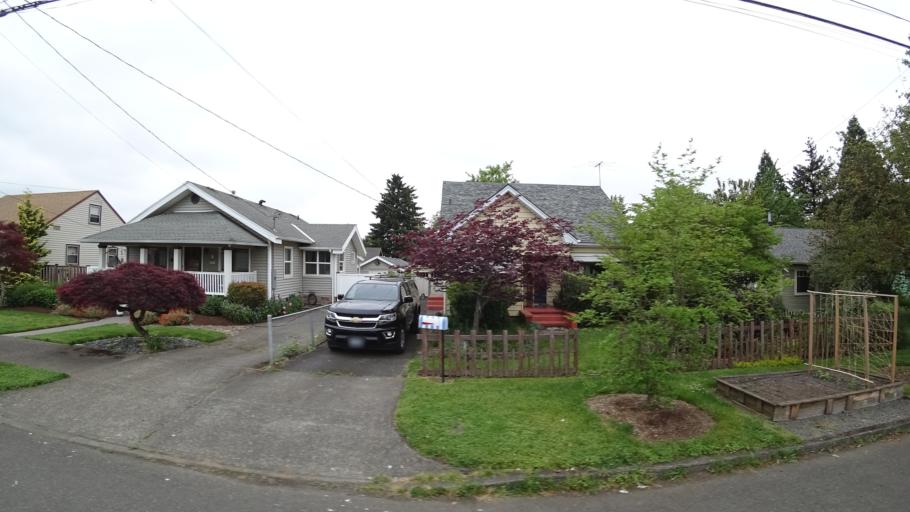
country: US
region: Oregon
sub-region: Multnomah County
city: Portland
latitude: 45.5575
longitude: -122.6169
